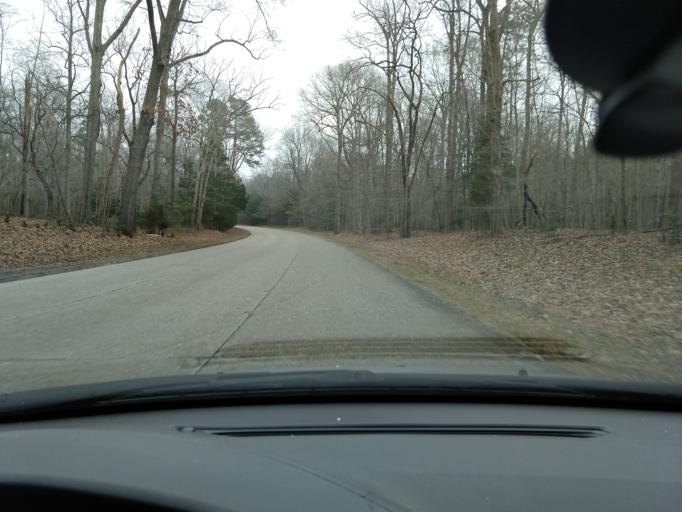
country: US
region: Virginia
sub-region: York County
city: Yorktown
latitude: 37.2712
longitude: -76.5952
